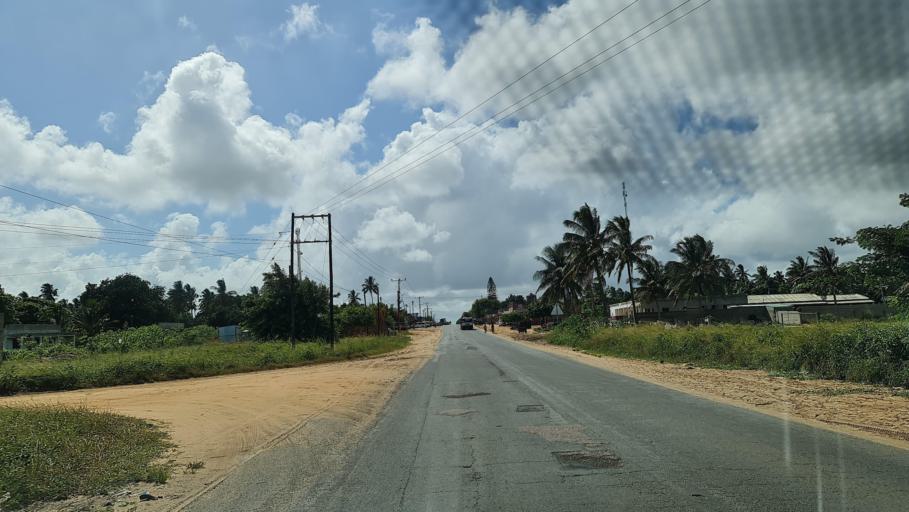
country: MZ
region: Gaza
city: Manjacaze
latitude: -24.6736
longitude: 34.5755
